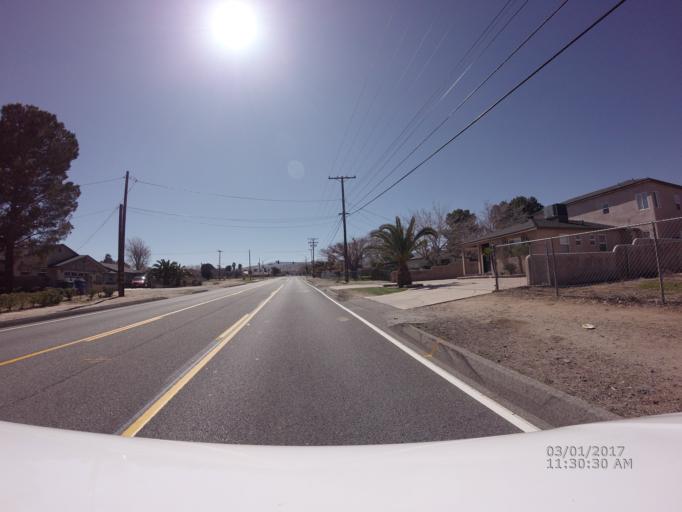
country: US
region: California
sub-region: Los Angeles County
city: Quartz Hill
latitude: 34.6394
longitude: -118.2187
